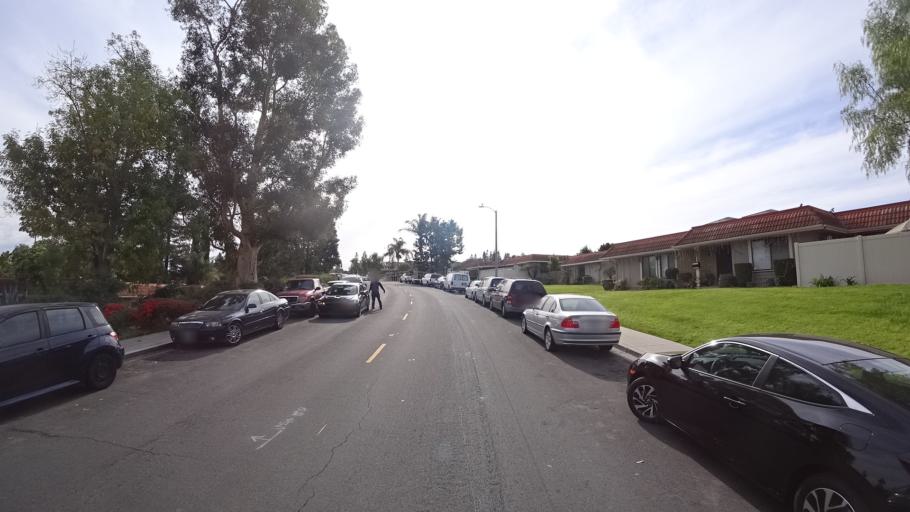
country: US
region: California
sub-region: Orange County
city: Laguna Woods
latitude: 33.6023
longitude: -117.7207
